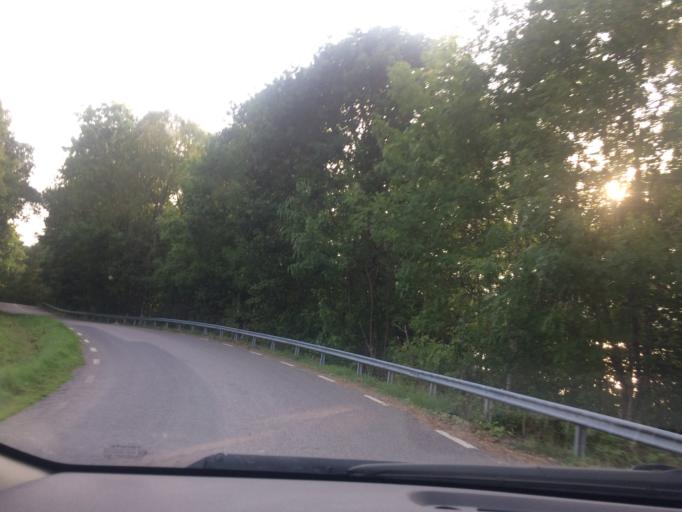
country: SE
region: Vaestra Goetaland
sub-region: Alingsas Kommun
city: Alingsas
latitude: 58.0096
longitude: 12.4913
